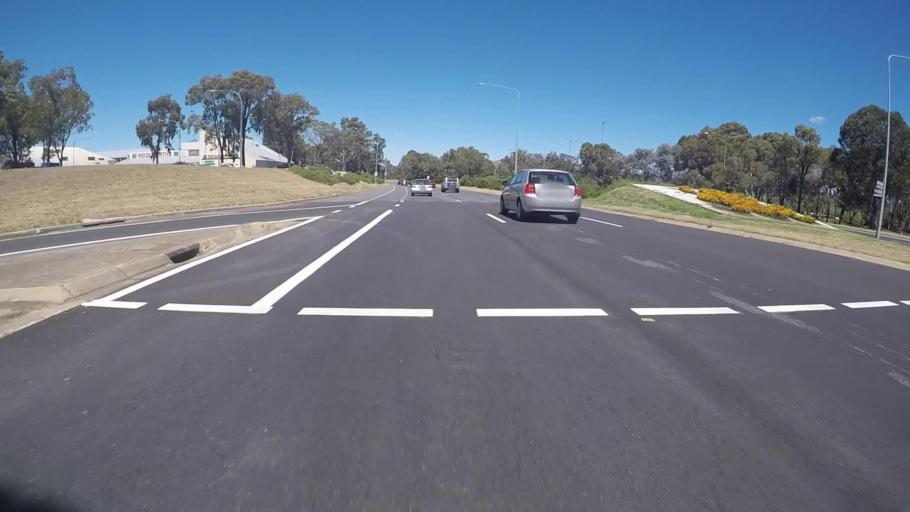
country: AU
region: Australian Capital Territory
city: Macarthur
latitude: -35.3794
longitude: 149.0566
